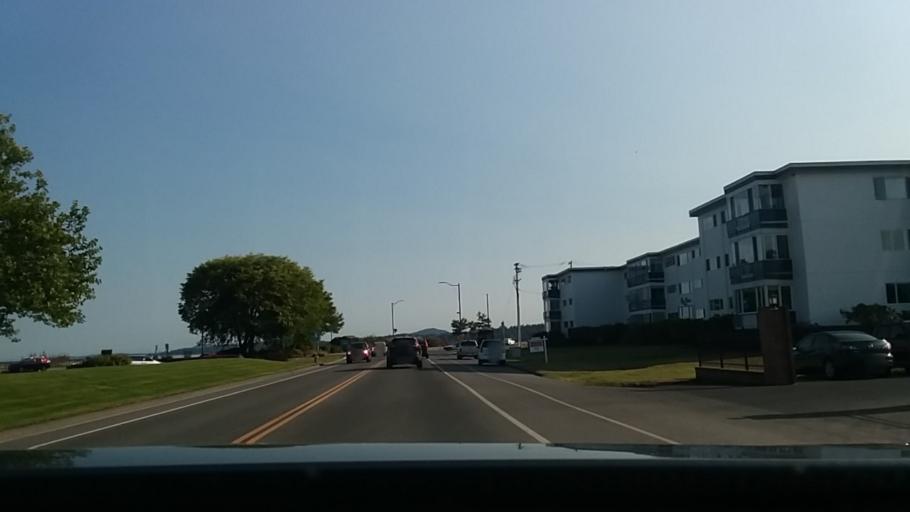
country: CA
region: British Columbia
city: North Saanich
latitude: 48.6425
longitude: -123.4004
